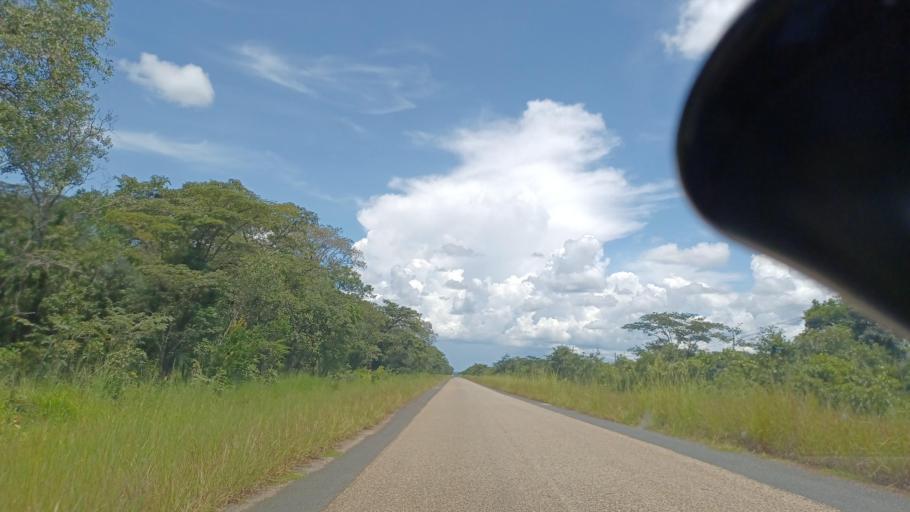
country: ZM
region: North-Western
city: Solwezi
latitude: -12.5806
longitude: 26.1306
